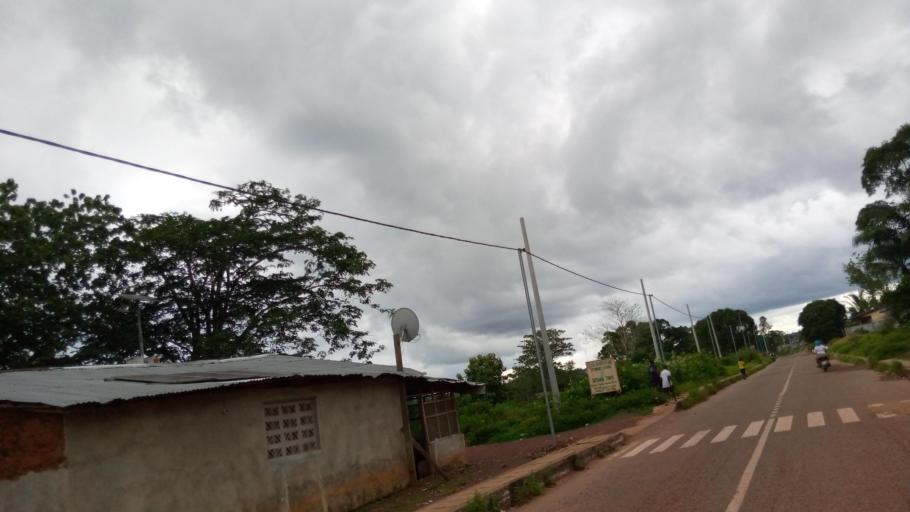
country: SL
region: Southern Province
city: Moyamba
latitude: 8.1637
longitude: -12.4431
